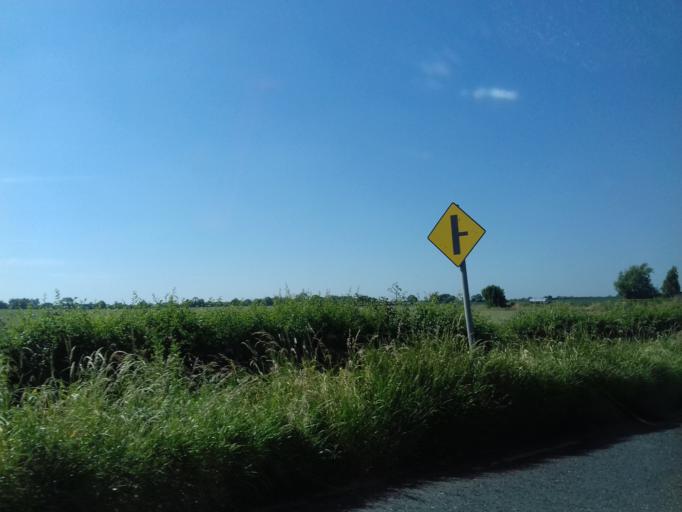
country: IE
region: Leinster
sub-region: Fingal County
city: Swords
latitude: 53.4919
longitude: -6.2690
